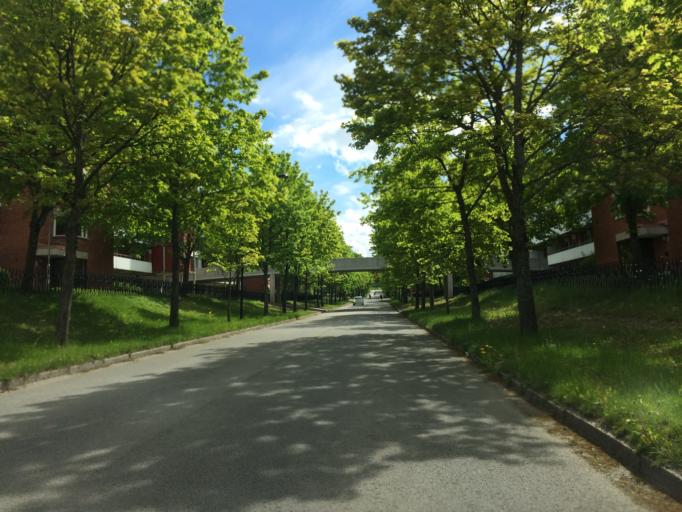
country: SE
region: Stockholm
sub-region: Botkyrka Kommun
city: Fittja
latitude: 59.2676
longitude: 17.8877
